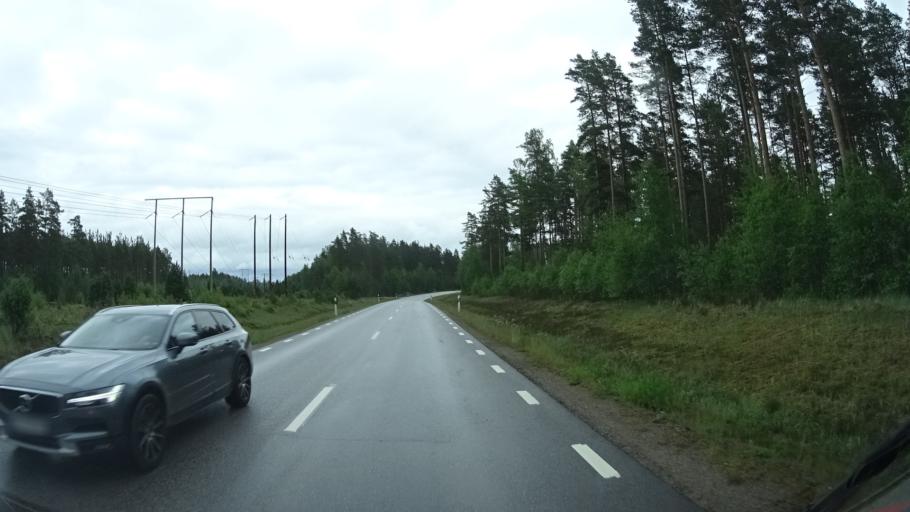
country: SE
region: Kalmar
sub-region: Hultsfreds Kommun
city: Hultsfred
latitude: 57.5131
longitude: 15.8286
